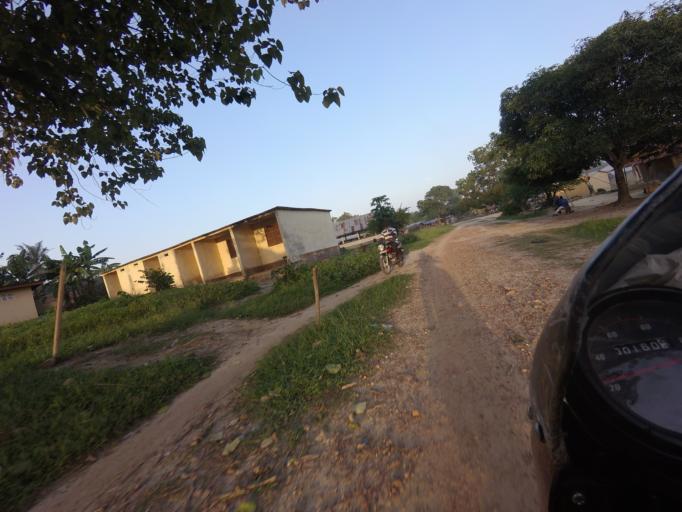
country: SL
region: Eastern Province
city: Tombu
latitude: 8.3972
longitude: -10.7064
